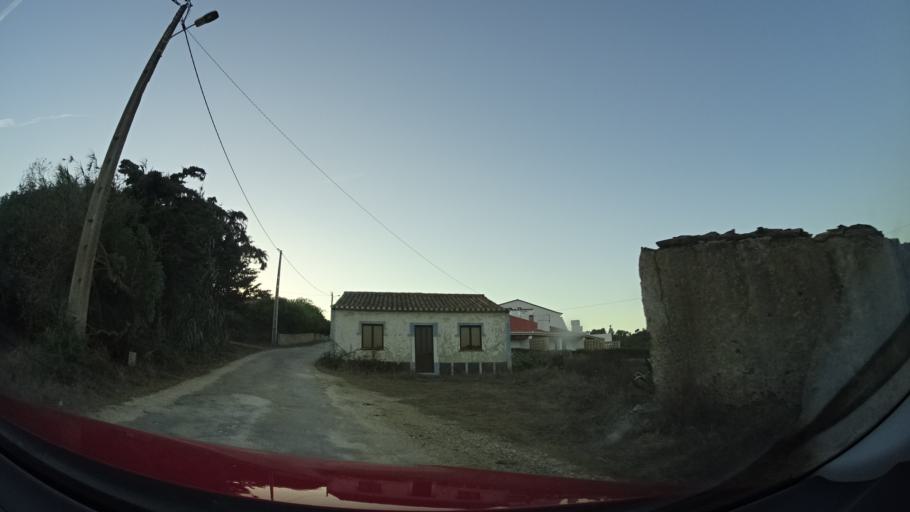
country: PT
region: Faro
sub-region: Aljezur
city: Aljezur
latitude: 37.2391
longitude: -8.8318
